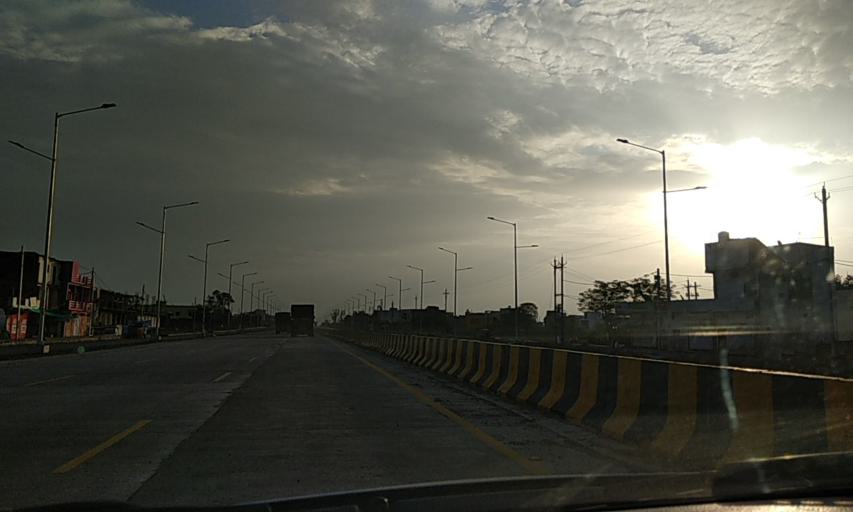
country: IN
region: Madhya Pradesh
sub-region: Rajgarh
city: Khujner
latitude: 23.7214
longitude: 76.7376
